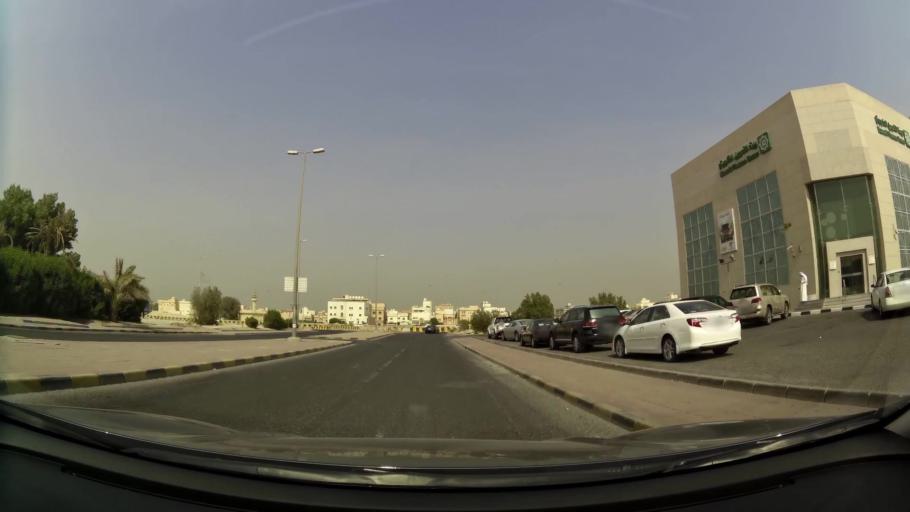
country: KW
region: Al Asimah
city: Ar Rabiyah
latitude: 29.3084
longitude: 47.8736
